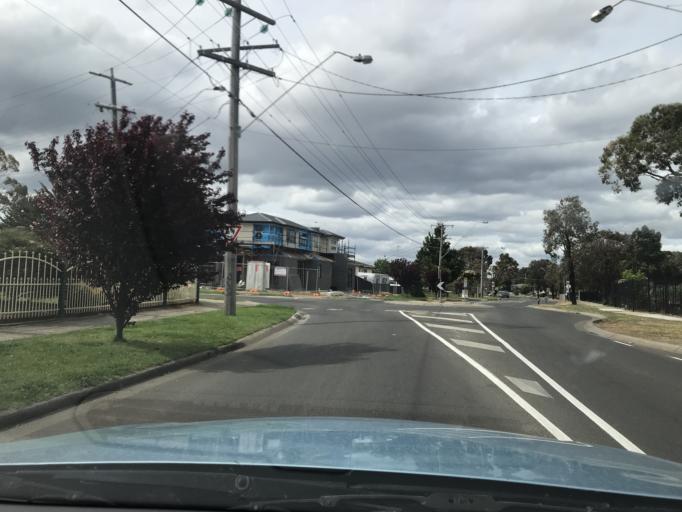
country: AU
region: Victoria
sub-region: Hobsons Bay
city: Laverton
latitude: -37.8564
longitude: 144.7716
